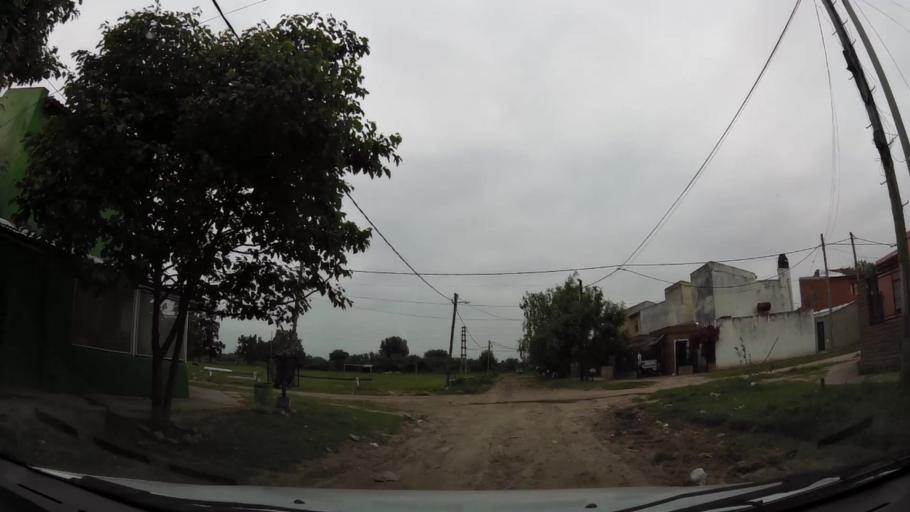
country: AR
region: Buenos Aires
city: San Justo
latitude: -34.6992
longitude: -58.5521
